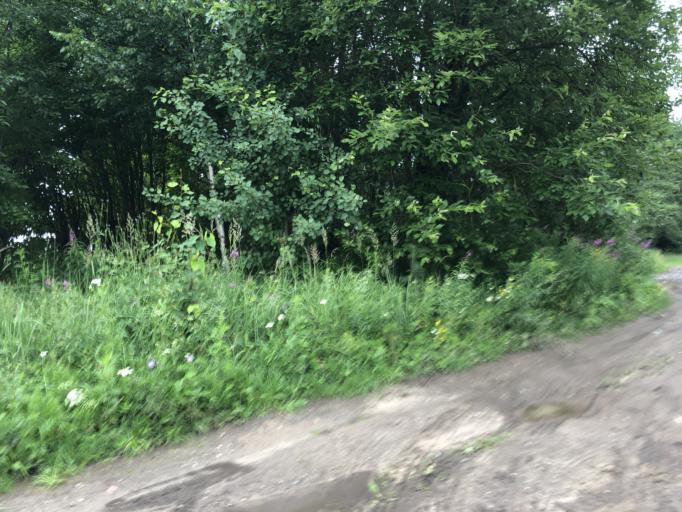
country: RU
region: Tverskaya
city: Rzhev
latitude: 56.2460
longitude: 34.3708
